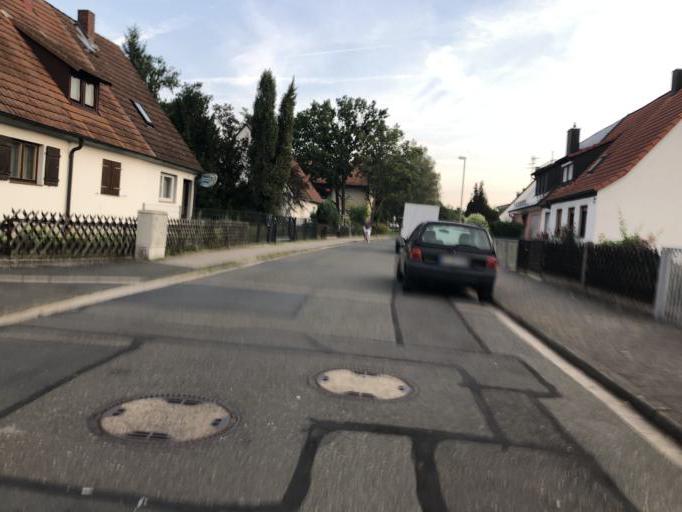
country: DE
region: Bavaria
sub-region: Regierungsbezirk Mittelfranken
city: Erlangen
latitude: 49.5920
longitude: 10.9780
